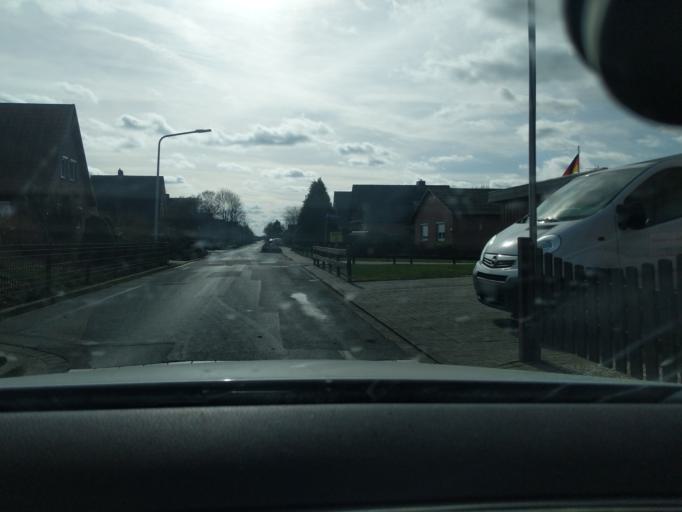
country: DE
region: Lower Saxony
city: Drochtersen
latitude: 53.6870
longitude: 9.4346
